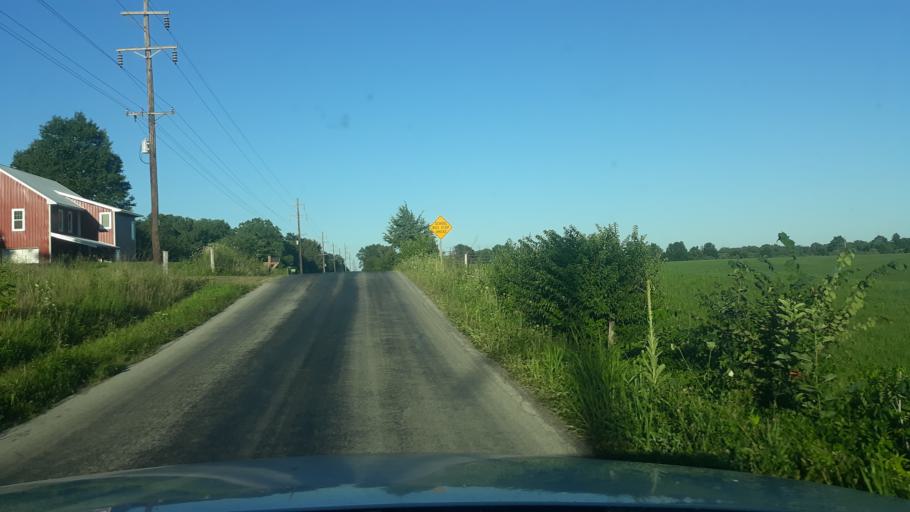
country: US
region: Illinois
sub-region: Saline County
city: Harrisburg
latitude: 37.8633
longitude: -88.6016
